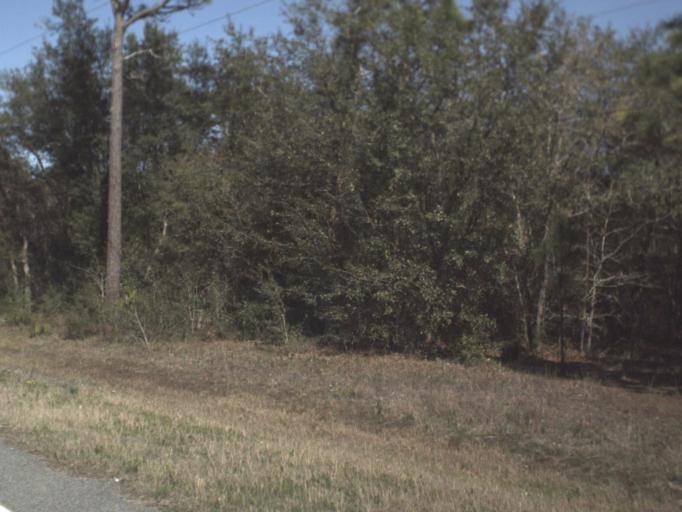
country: US
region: Florida
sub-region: Wakulla County
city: Crawfordville
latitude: 29.9413
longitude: -84.3879
